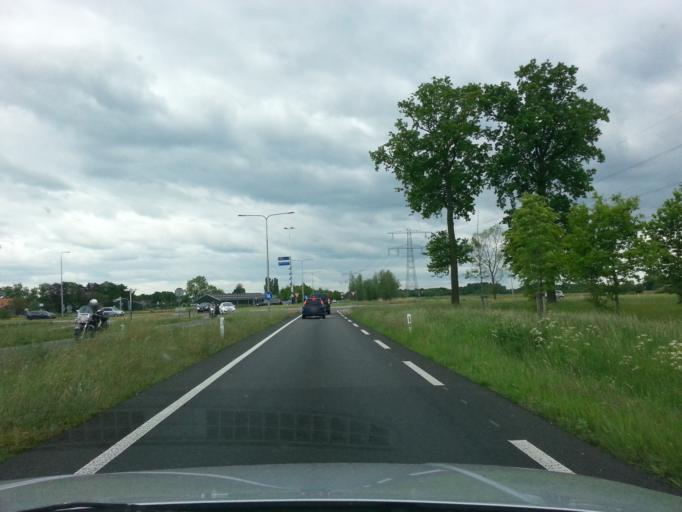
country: NL
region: Gelderland
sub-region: Gemeente Zutphen
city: Leesten
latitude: 52.1346
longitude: 6.2590
